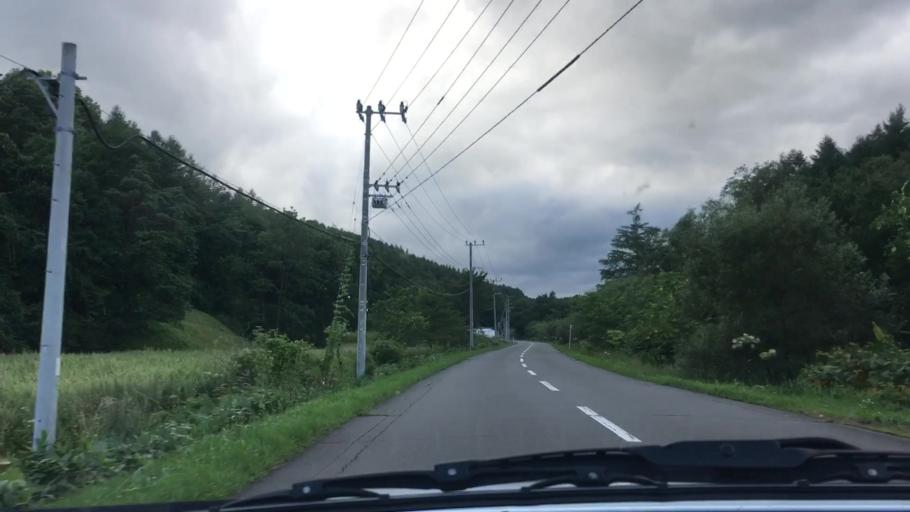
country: JP
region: Hokkaido
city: Otofuke
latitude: 43.1421
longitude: 142.8836
